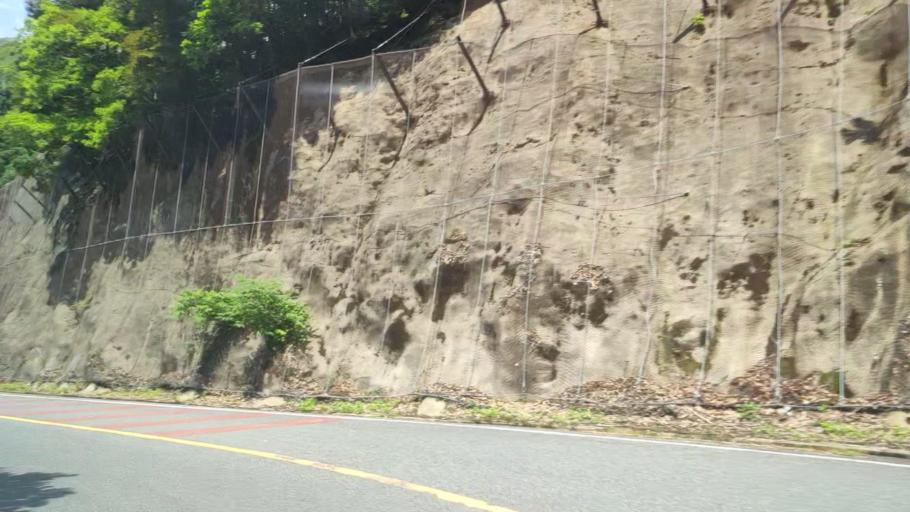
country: JP
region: Hyogo
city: Toyooka
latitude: 35.6365
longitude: 134.7807
